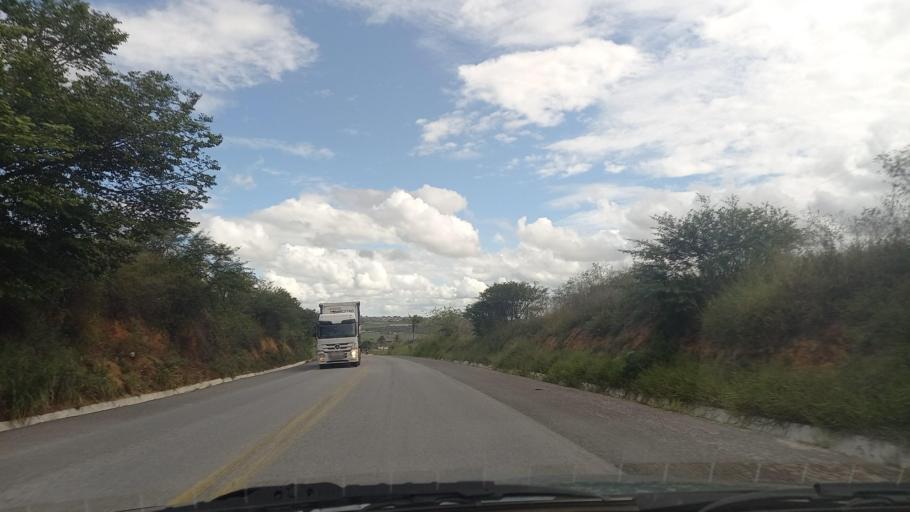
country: BR
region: Pernambuco
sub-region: Lajedo
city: Lajedo
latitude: -8.6846
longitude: -36.4082
